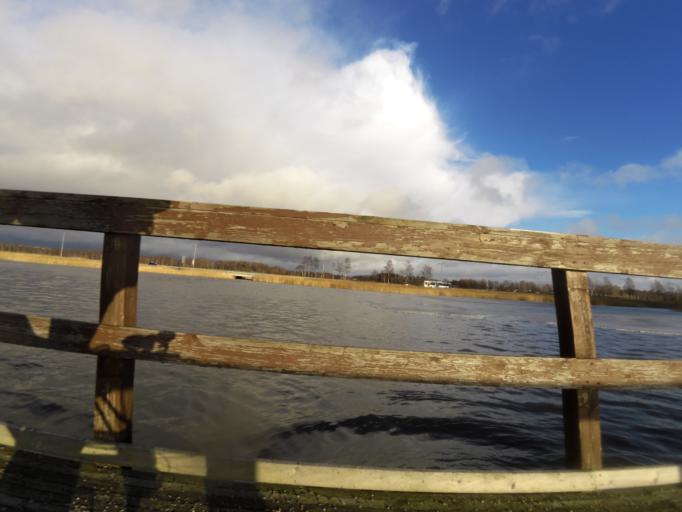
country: FI
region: Uusimaa
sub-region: Helsinki
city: Teekkarikylae
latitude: 60.2045
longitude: 24.8439
